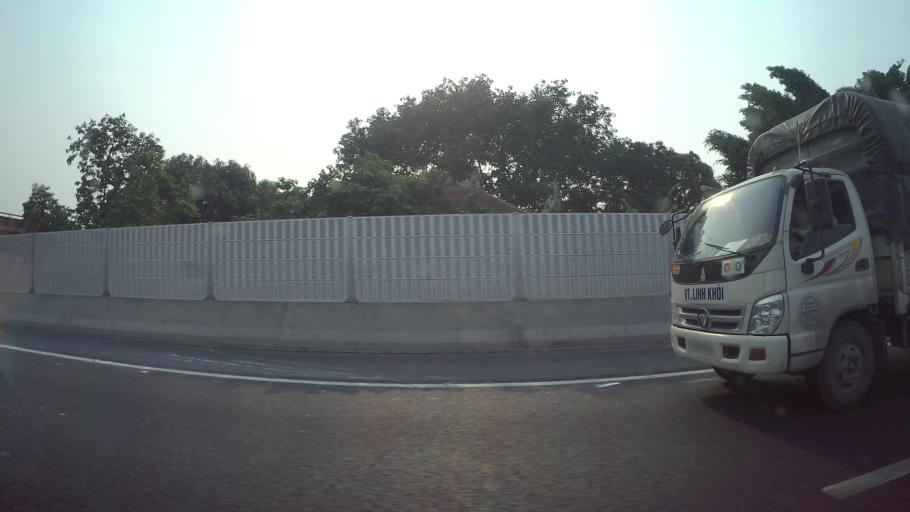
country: VN
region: Ha Noi
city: Van Dien
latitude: 20.9219
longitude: 105.8598
